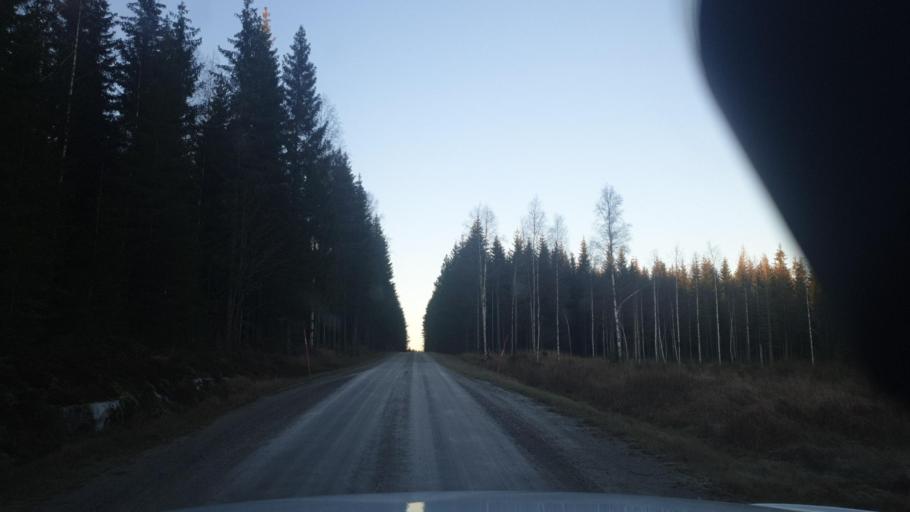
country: SE
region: Vaermland
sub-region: Eda Kommun
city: Charlottenberg
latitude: 60.0102
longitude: 12.5061
